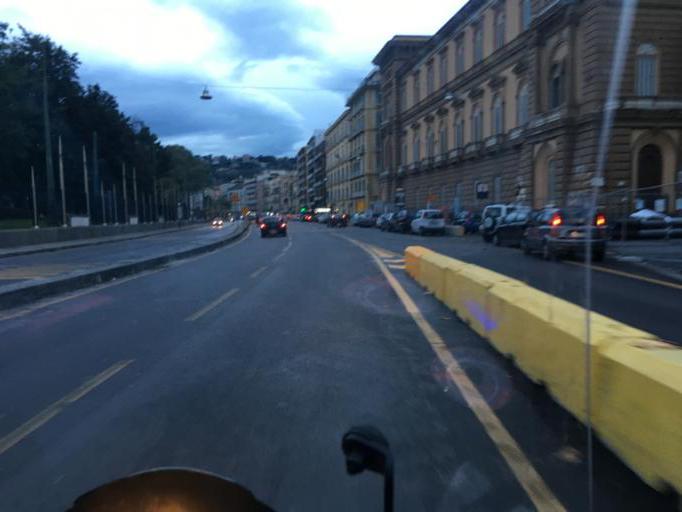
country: IT
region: Campania
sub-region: Provincia di Napoli
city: Napoli
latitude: 40.8337
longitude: 14.2338
